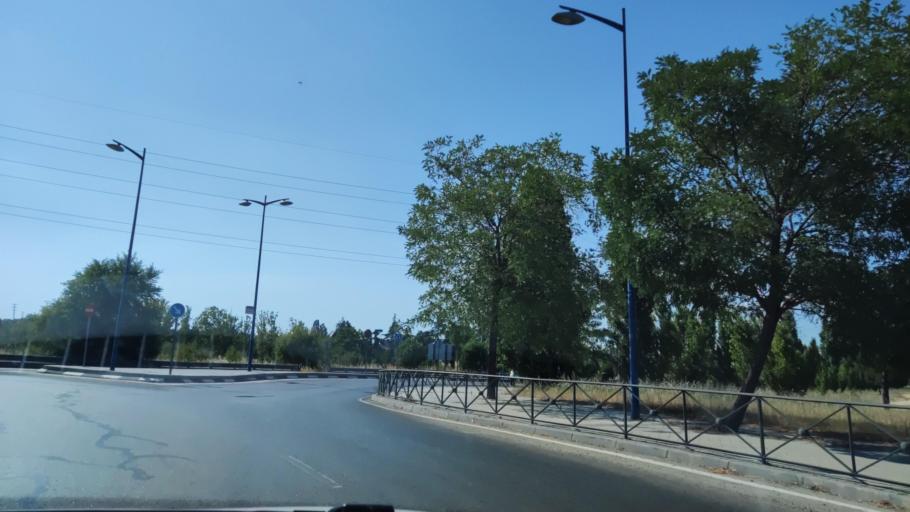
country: ES
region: Madrid
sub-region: Provincia de Madrid
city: Leganes
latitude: 40.3381
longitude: -3.7871
